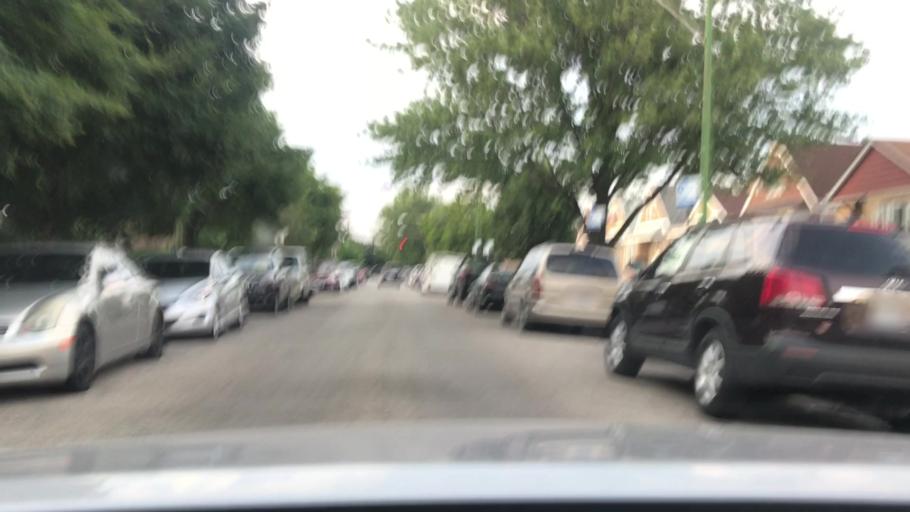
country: US
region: Illinois
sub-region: Cook County
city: Hometown
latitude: 41.7629
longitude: -87.7175
